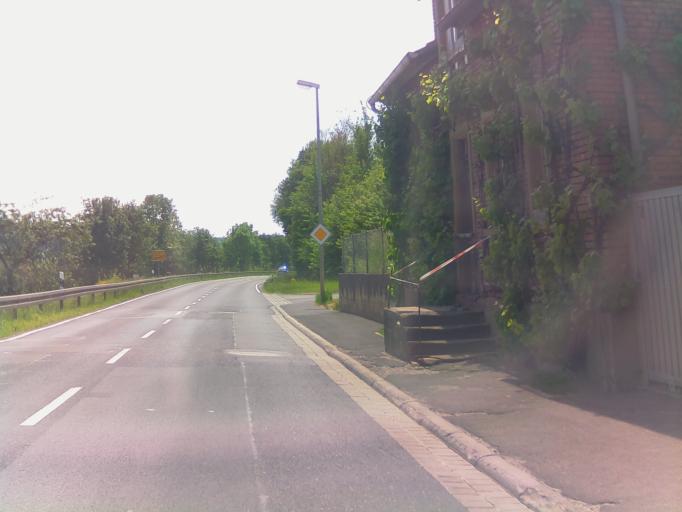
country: DE
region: Bavaria
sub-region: Regierungsbezirk Unterfranken
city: Thungen
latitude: 49.9597
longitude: 9.8960
